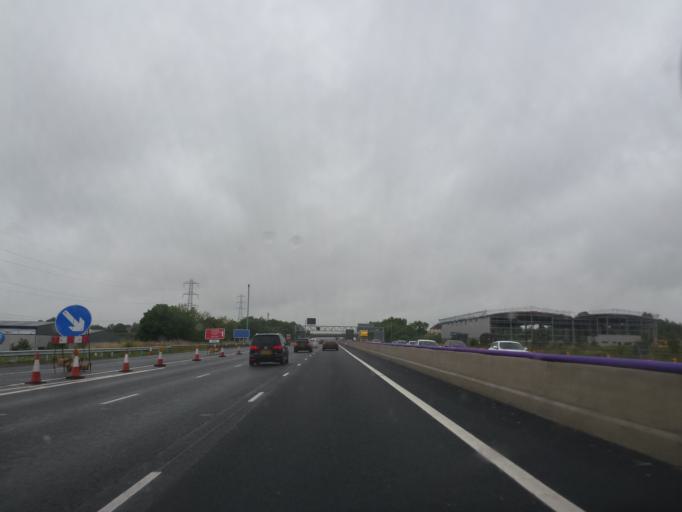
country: GB
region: England
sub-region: Derbyshire
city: Staveley
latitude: 53.2409
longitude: -1.3325
